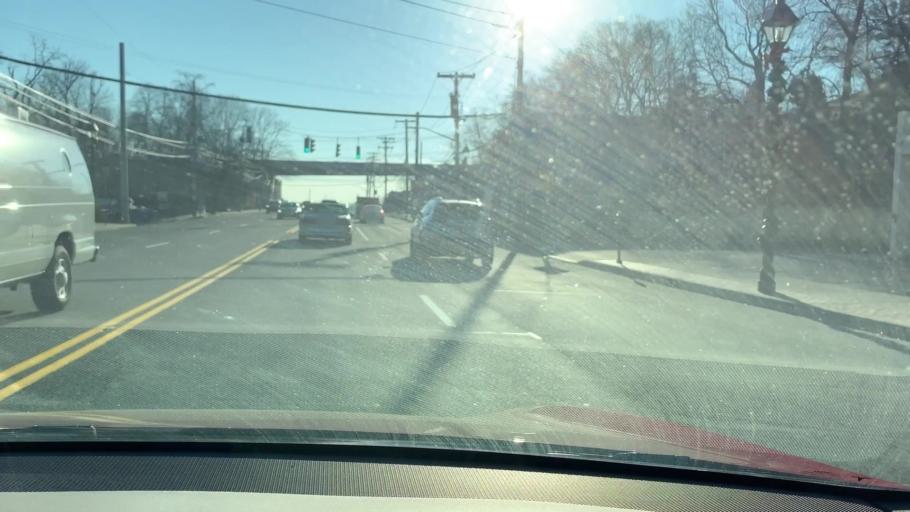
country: US
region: New York
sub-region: Westchester County
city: Elmsford
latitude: 41.0516
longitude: -73.8132
